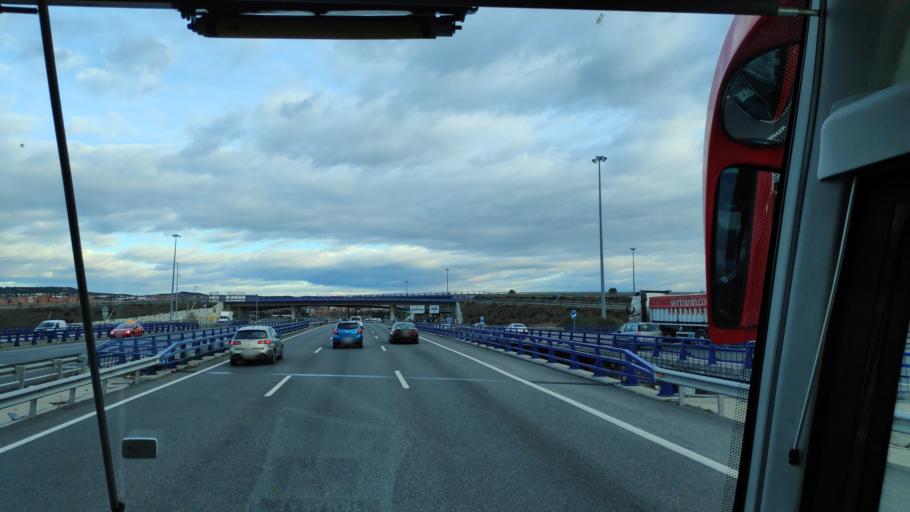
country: ES
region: Madrid
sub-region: Provincia de Madrid
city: Villa de Vallecas
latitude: 40.3602
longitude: -3.5660
